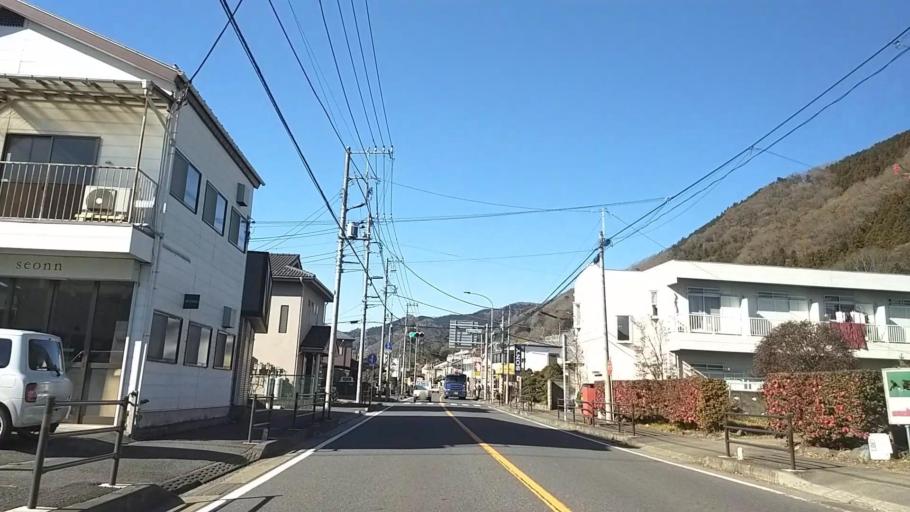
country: JP
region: Yamanashi
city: Uenohara
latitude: 35.6166
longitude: 139.1878
